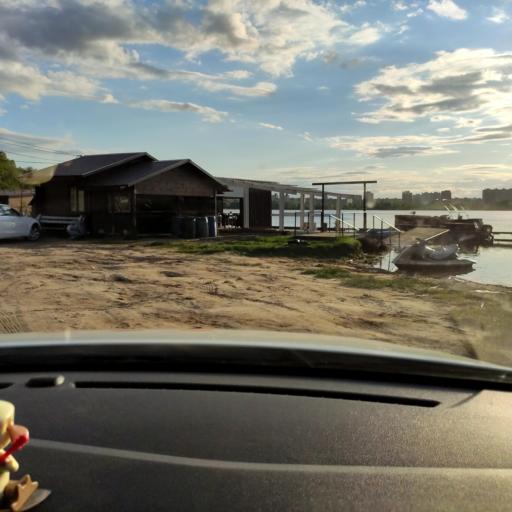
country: RU
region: Tatarstan
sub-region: Gorod Kazan'
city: Kazan
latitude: 55.8335
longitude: 49.1828
